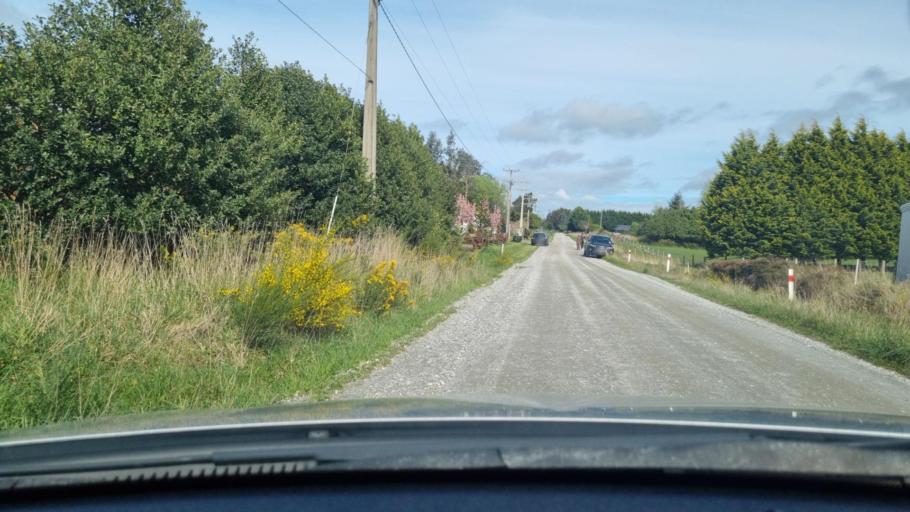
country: NZ
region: Southland
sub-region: Invercargill City
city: Invercargill
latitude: -46.4516
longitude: 168.3773
